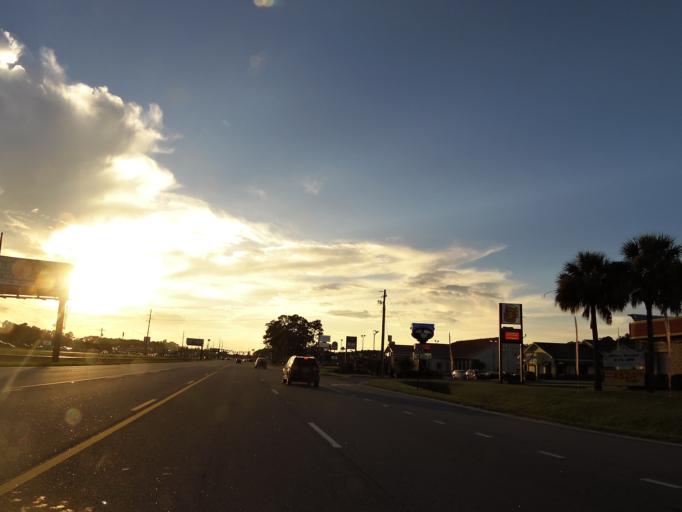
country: US
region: Georgia
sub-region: Camden County
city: Kingsland
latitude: 30.7876
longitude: -81.6489
